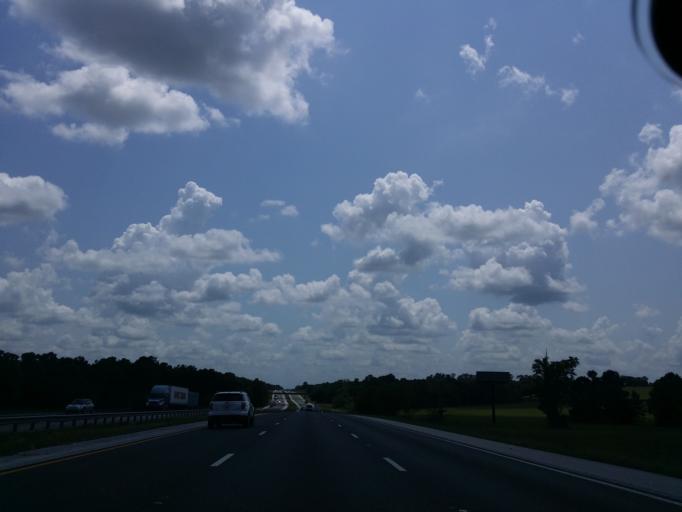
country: US
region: Florida
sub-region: Marion County
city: Citra
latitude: 29.3303
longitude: -82.2144
